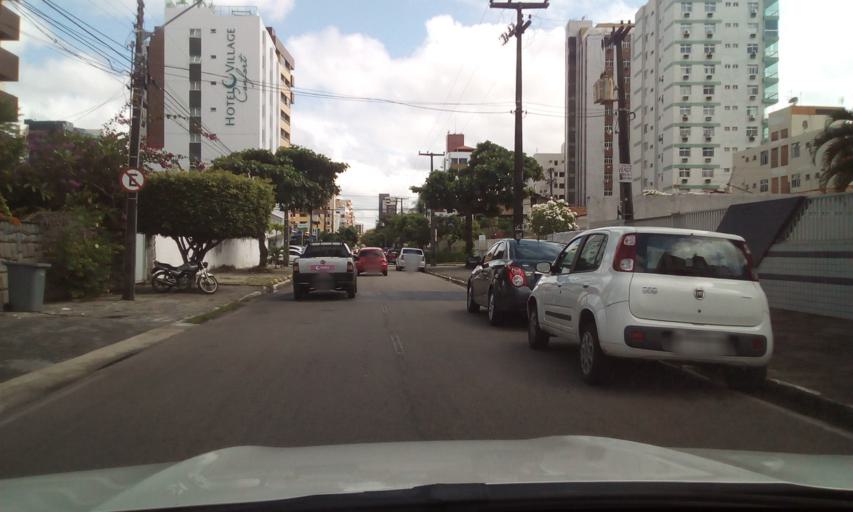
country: BR
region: Paraiba
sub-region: Joao Pessoa
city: Joao Pessoa
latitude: -7.1043
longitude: -34.8323
